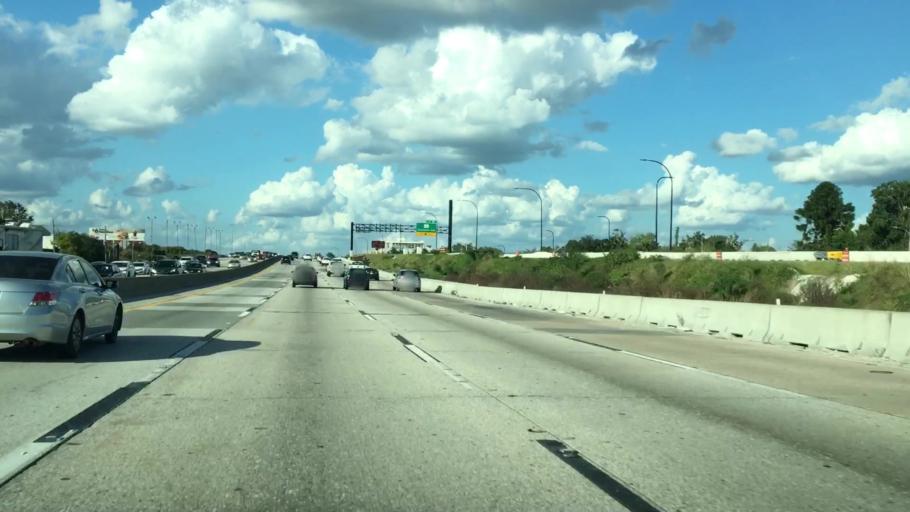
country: US
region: Florida
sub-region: Orange County
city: Fairview Shores
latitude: 28.5794
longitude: -81.3752
